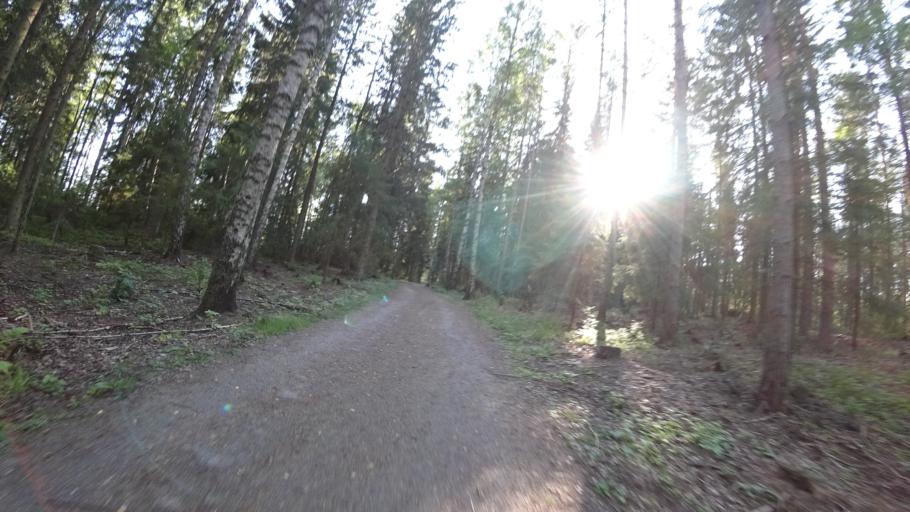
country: FI
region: Pirkanmaa
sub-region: Tampere
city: Pirkkala
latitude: 61.4969
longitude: 23.6100
